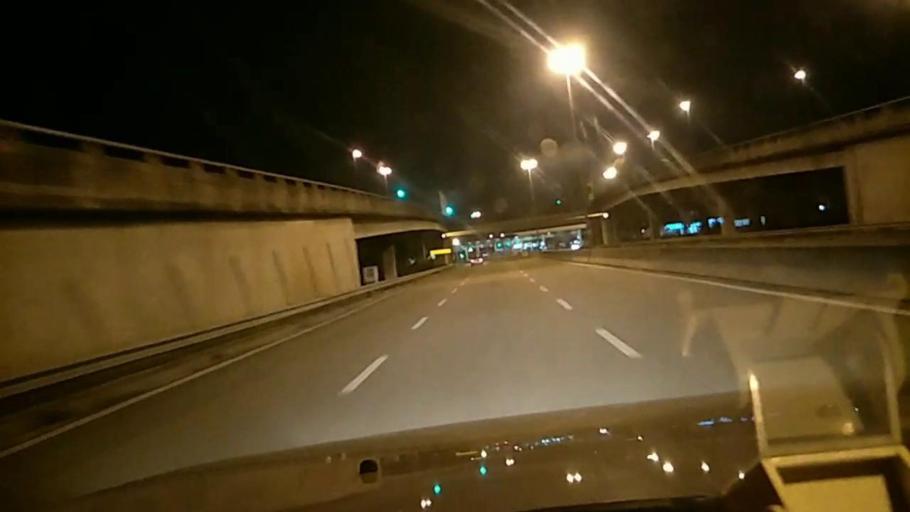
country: MY
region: Penang
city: Perai
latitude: 5.3841
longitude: 100.3883
